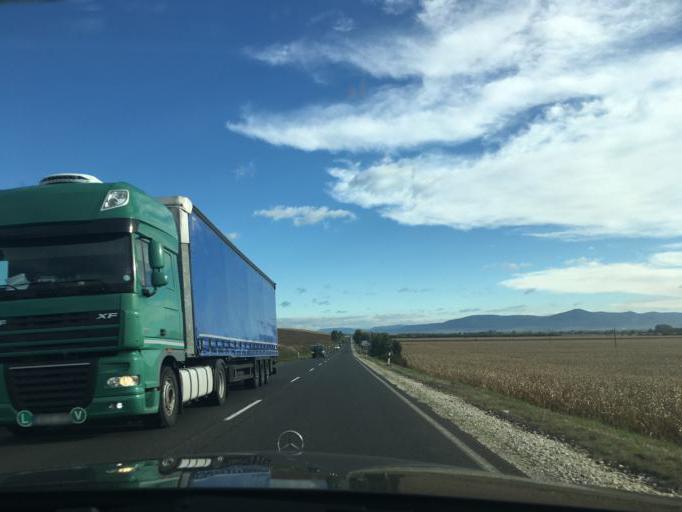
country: HU
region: Borsod-Abauj-Zemplen
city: Encs
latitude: 48.3416
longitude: 21.1146
